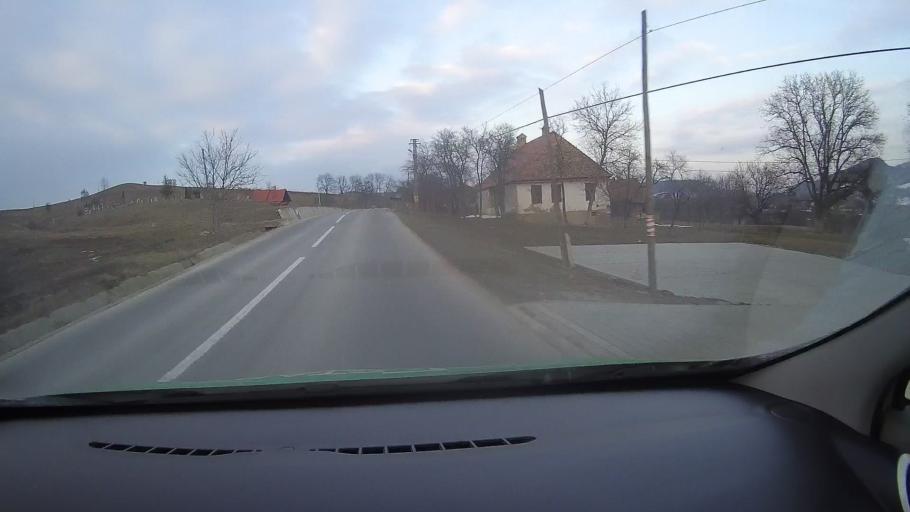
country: RO
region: Harghita
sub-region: Comuna Lupeni
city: Lupeni
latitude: 46.3587
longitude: 25.1689
